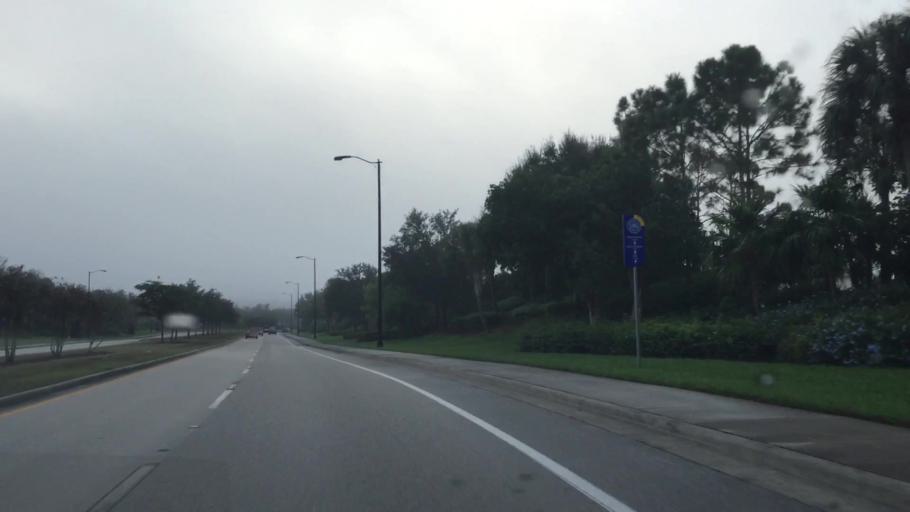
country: US
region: Florida
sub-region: Lee County
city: Gateway
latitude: 26.5815
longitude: -81.7827
